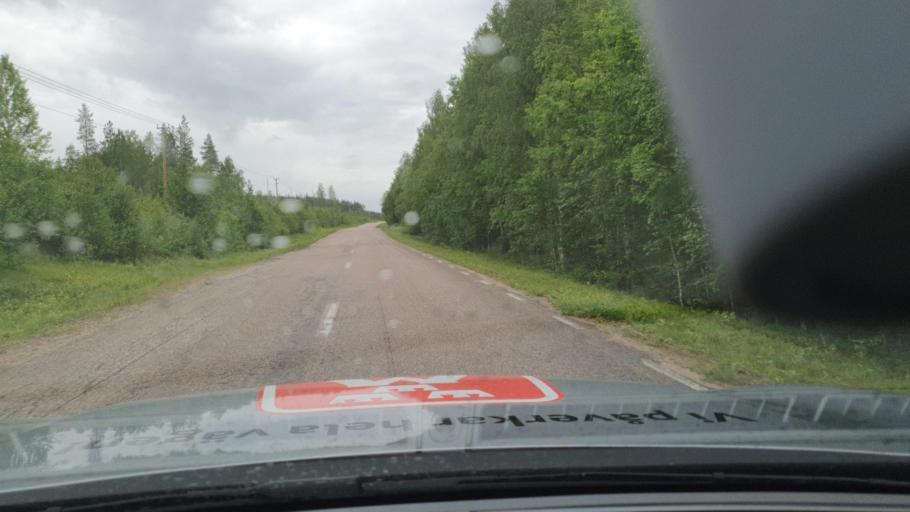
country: SE
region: Norrbotten
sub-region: Overkalix Kommun
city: OEverkalix
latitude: 66.4420
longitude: 22.7729
